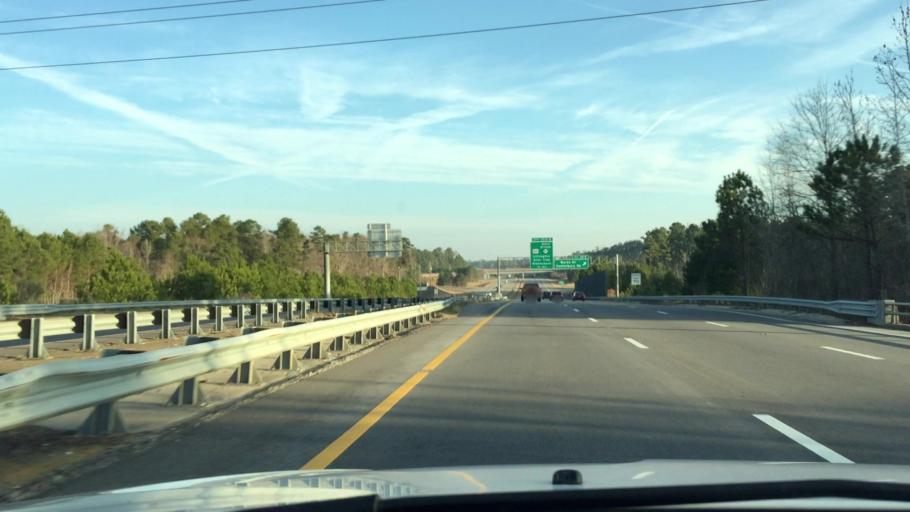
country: US
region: North Carolina
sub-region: Lee County
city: Sanford
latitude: 35.4959
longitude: -79.1949
